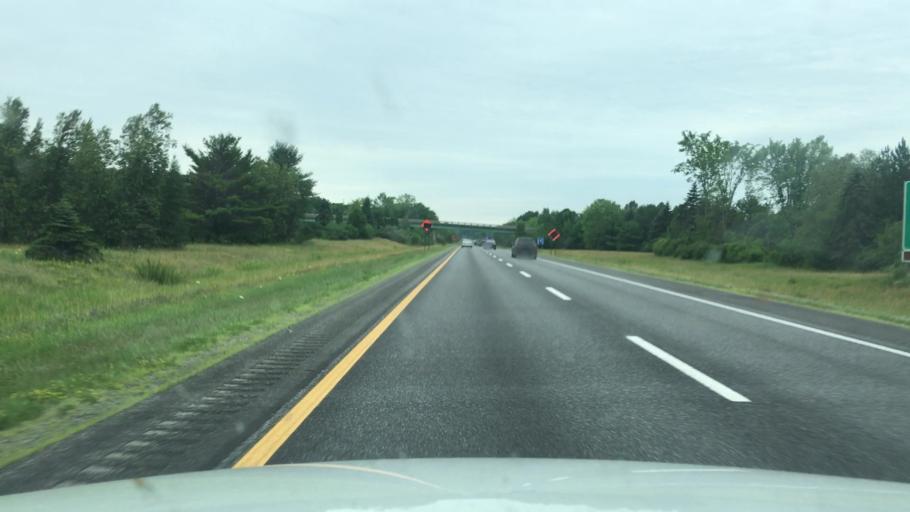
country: US
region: Maine
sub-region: Sagadahoc County
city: Richmond
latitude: 44.1161
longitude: -69.8562
